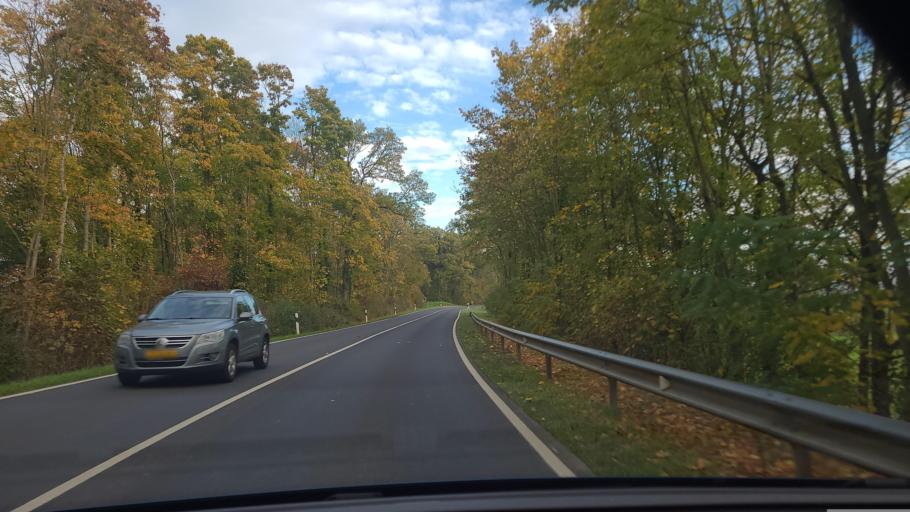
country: LU
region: Luxembourg
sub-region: Canton de Capellen
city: Garnich
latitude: 49.6241
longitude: 5.9521
